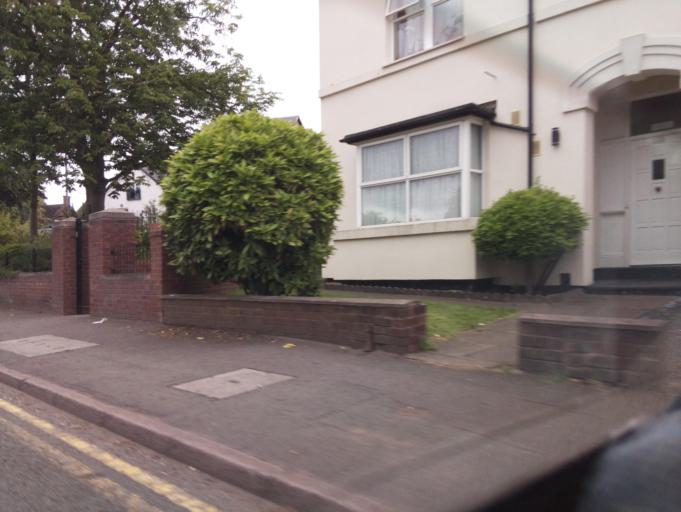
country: GB
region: England
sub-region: Wolverhampton
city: Wolverhampton
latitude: 52.5667
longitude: -2.1457
